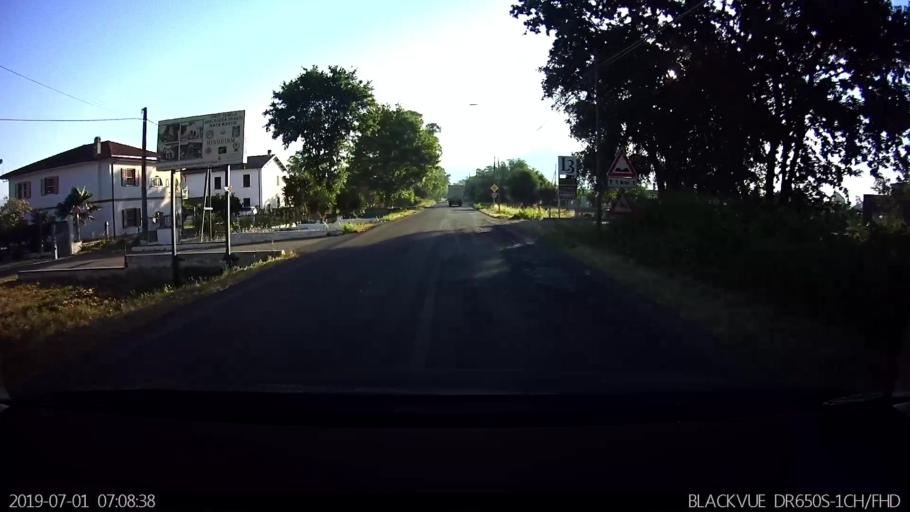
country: IT
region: Latium
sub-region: Provincia di Latina
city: Borgo Hermada
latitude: 41.2990
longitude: 13.1525
